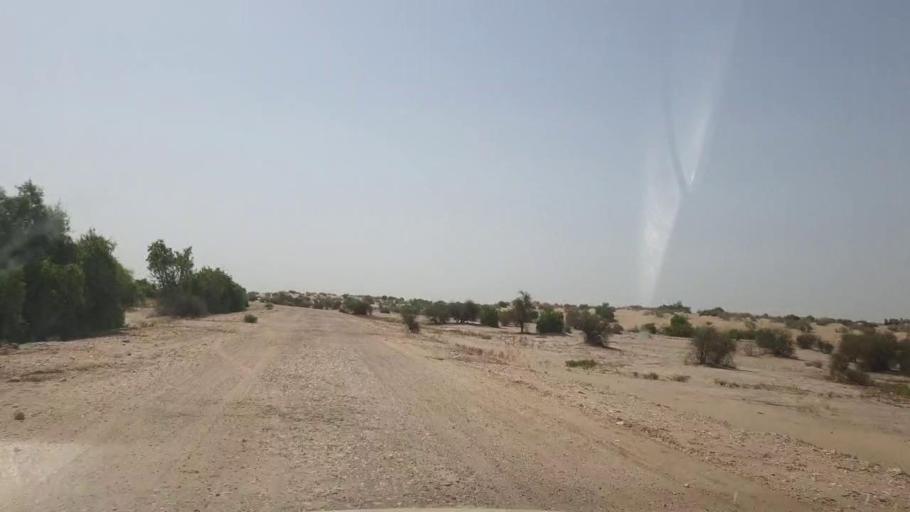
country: PK
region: Sindh
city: Rohri
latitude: 27.4378
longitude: 69.2446
